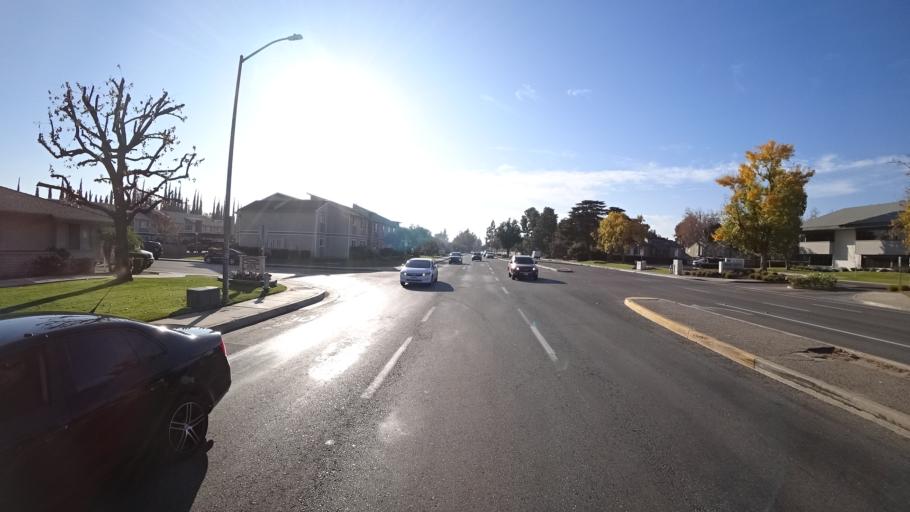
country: US
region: California
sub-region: Kern County
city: Bakersfield
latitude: 35.3373
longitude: -119.0631
